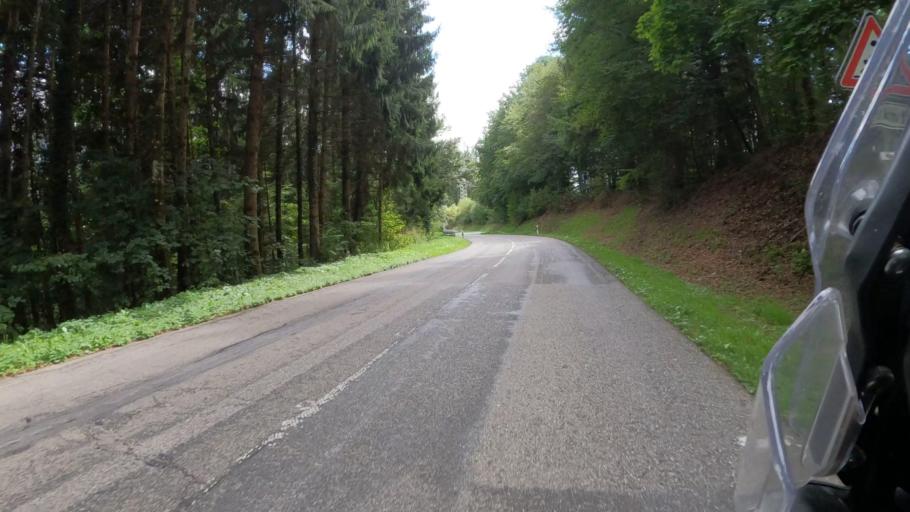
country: DE
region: Baden-Wuerttemberg
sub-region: Freiburg Region
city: Weilheim
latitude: 47.6865
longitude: 8.2558
